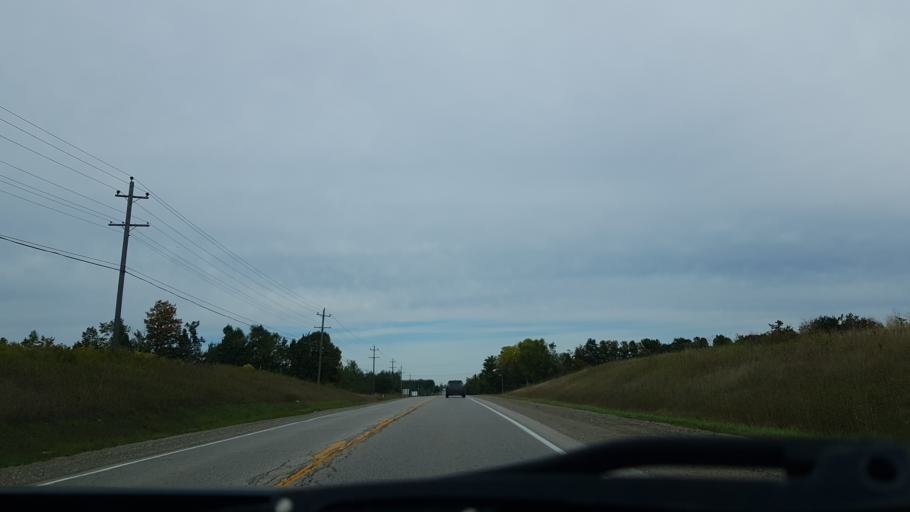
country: CA
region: Ontario
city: Orangeville
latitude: 43.7976
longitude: -80.0648
